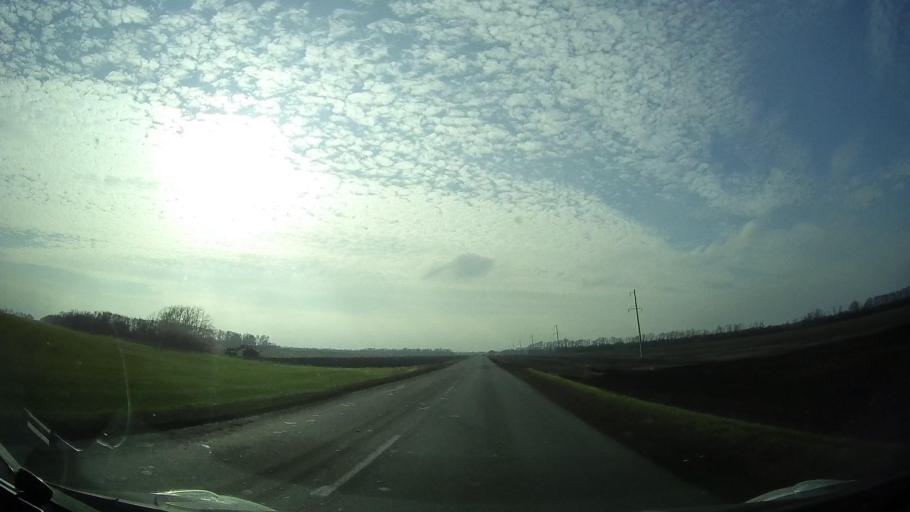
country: RU
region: Rostov
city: Mechetinskaya
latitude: 46.8043
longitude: 40.5230
